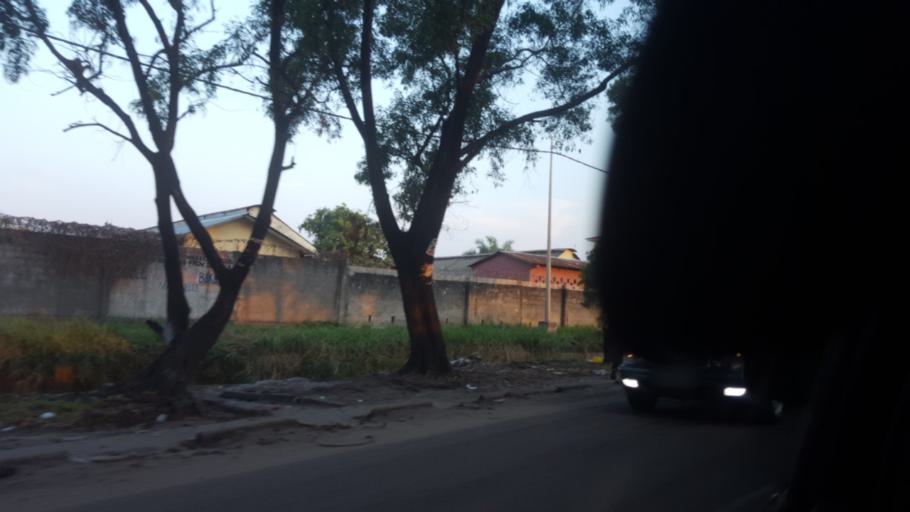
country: CD
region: Kinshasa
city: Kinshasa
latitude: -4.3412
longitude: 15.3205
